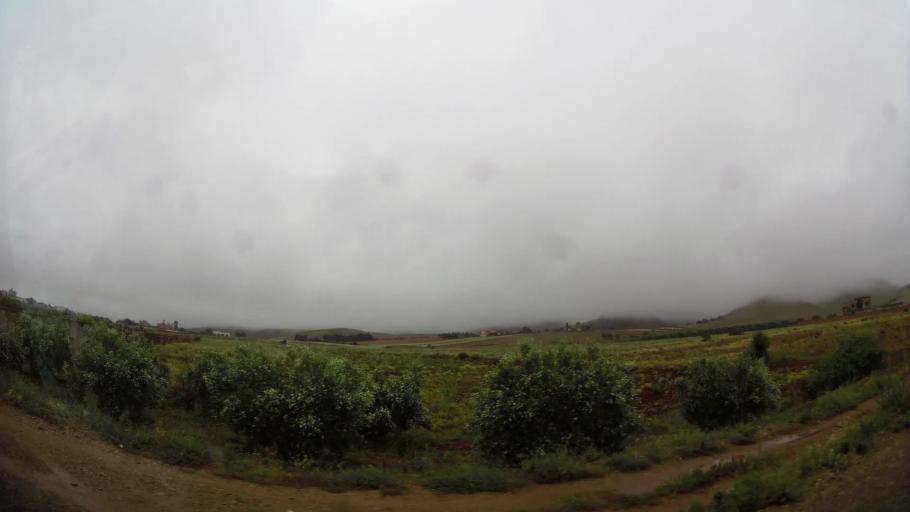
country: MA
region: Oriental
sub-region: Nador
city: Boudinar
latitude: 35.1147
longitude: -3.5759
